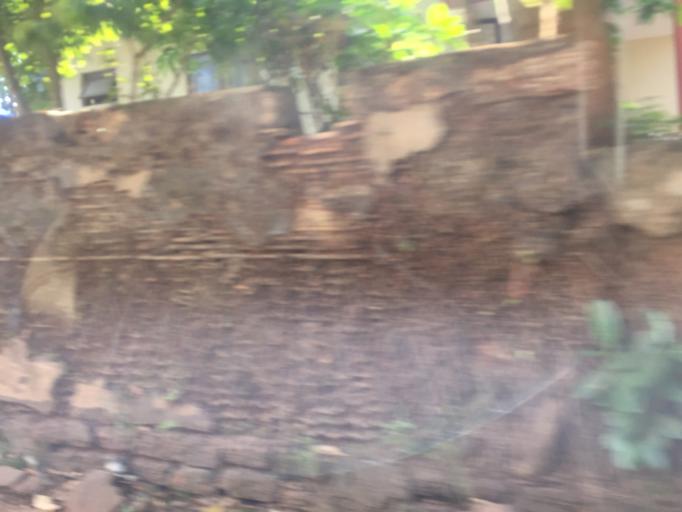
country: IN
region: Karnataka
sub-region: Dakshina Kannada
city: Ullal
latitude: 12.8485
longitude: 74.8422
